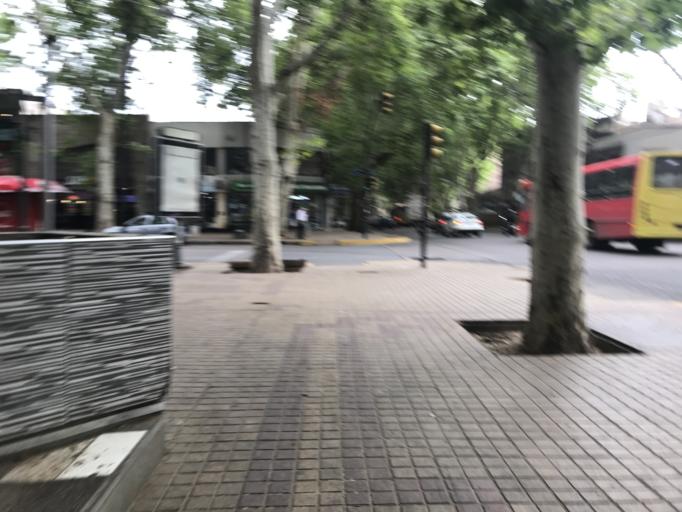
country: AR
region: Mendoza
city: Mendoza
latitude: -32.8856
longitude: -68.8448
